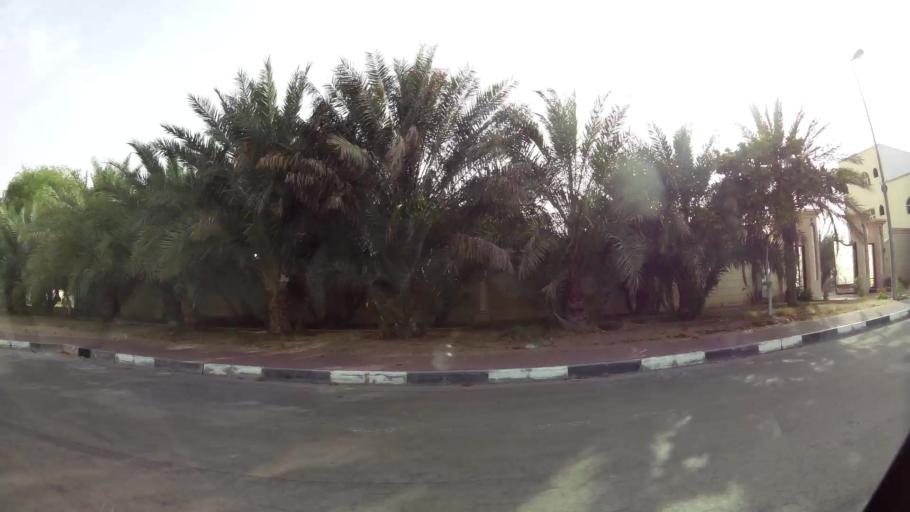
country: AE
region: Abu Dhabi
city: Al Ain
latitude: 24.2158
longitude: 55.6441
